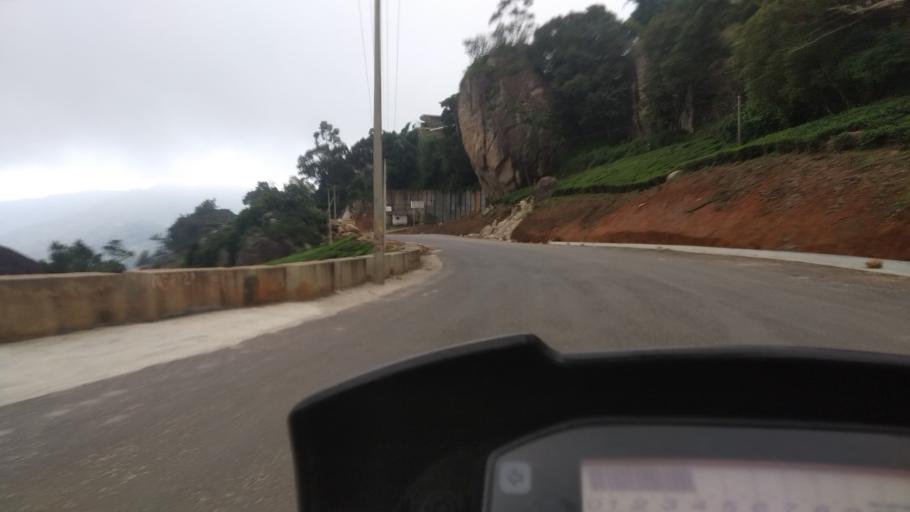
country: IN
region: Kerala
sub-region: Idukki
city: Munnar
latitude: 10.0327
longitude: 77.1604
